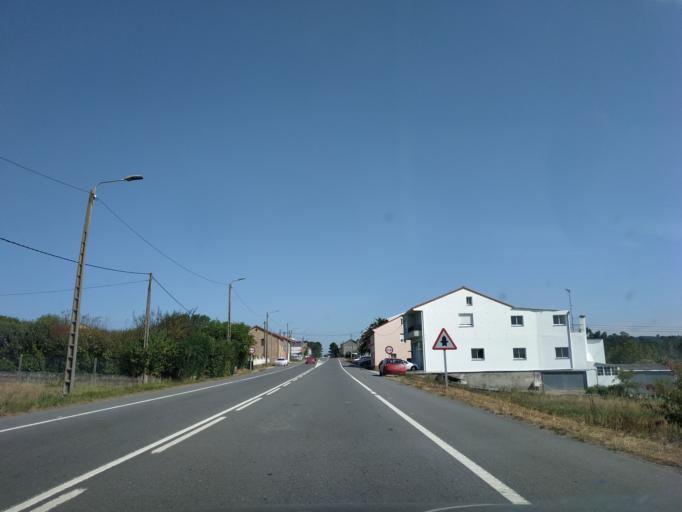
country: ES
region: Galicia
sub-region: Provincia da Coruna
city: Carballo
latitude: 43.2300
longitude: -8.6667
